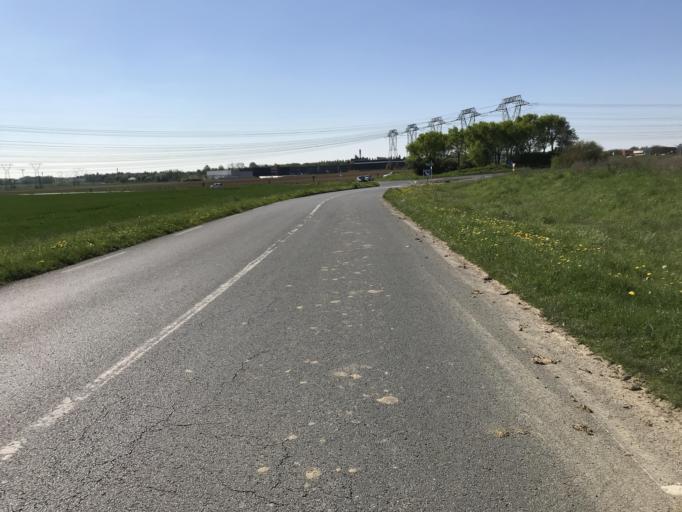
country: FR
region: Ile-de-France
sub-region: Departement de l'Essonne
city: Villejust
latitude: 48.6816
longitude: 2.2306
